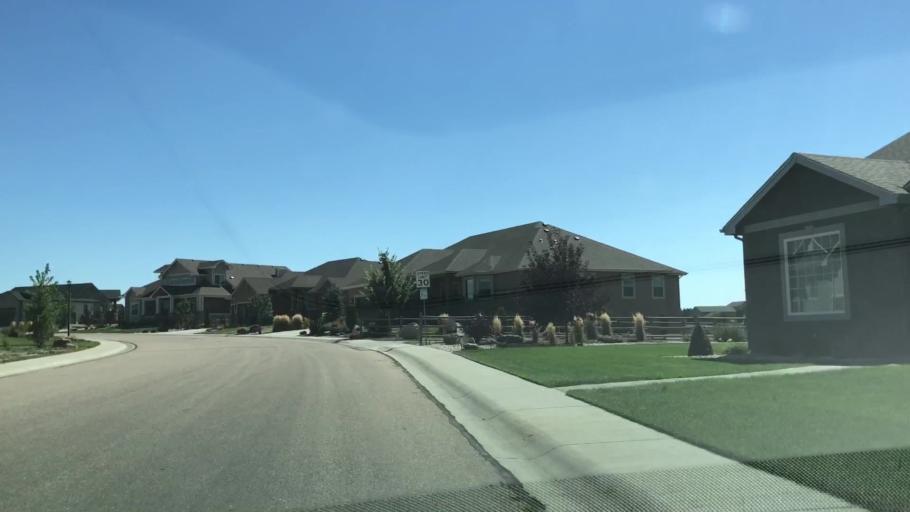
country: US
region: Colorado
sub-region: Weld County
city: Windsor
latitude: 40.4518
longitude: -104.9602
